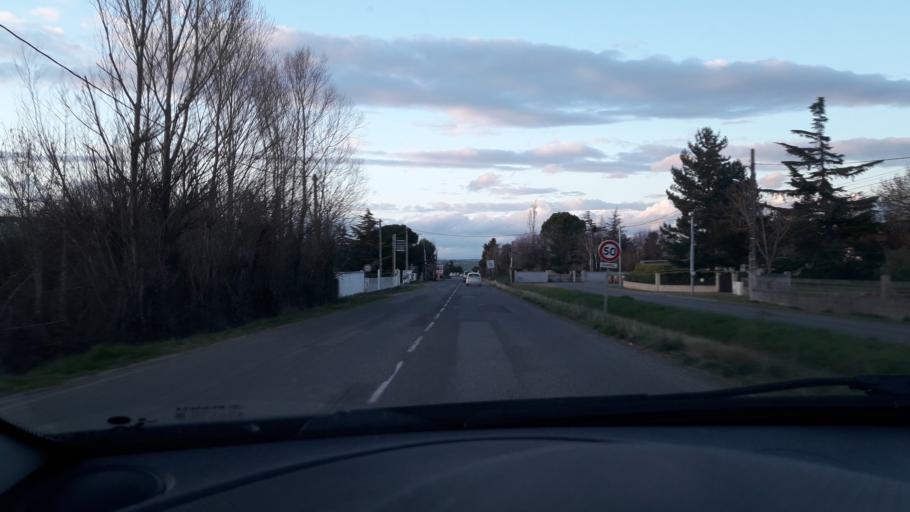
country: FR
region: Midi-Pyrenees
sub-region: Departement du Gers
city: Pujaudran
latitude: 43.6063
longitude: 1.1006
